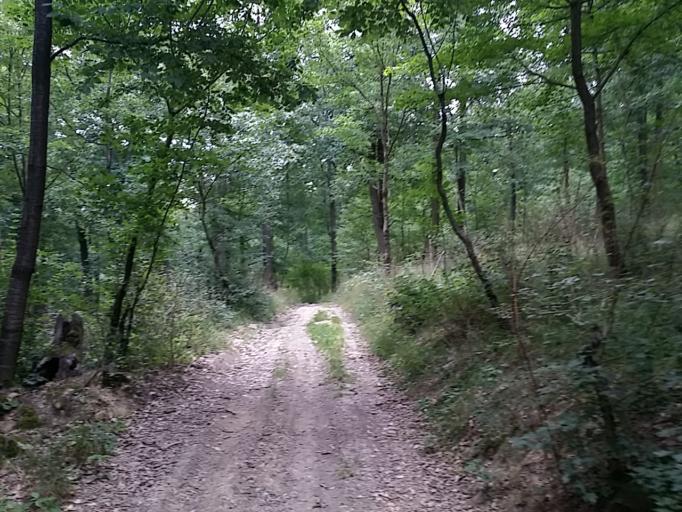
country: HU
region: Pest
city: Csobanka
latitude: 47.6536
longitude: 18.9439
